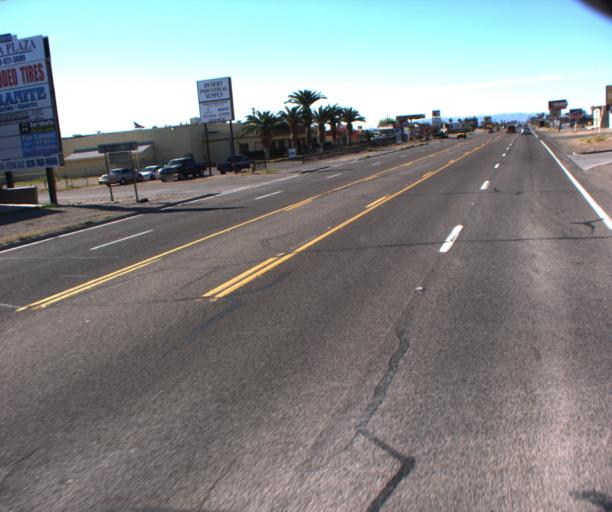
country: US
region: Arizona
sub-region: Mohave County
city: Mohave Valley
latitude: 35.0109
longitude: -114.5981
